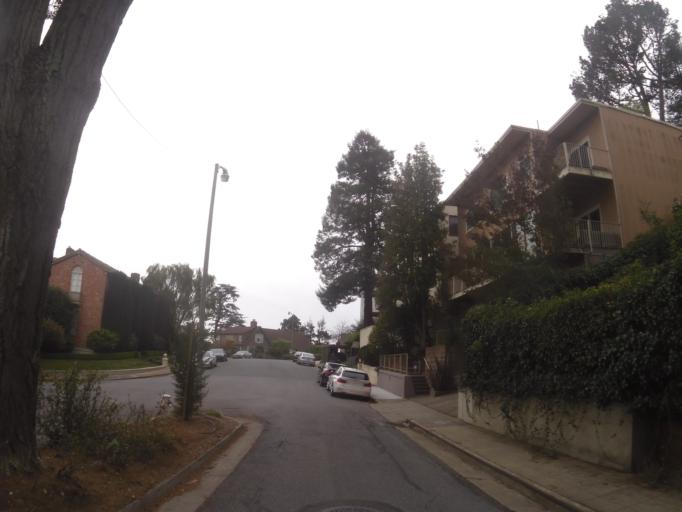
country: US
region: California
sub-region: San Mateo County
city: Daly City
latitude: 37.7482
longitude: -122.4651
